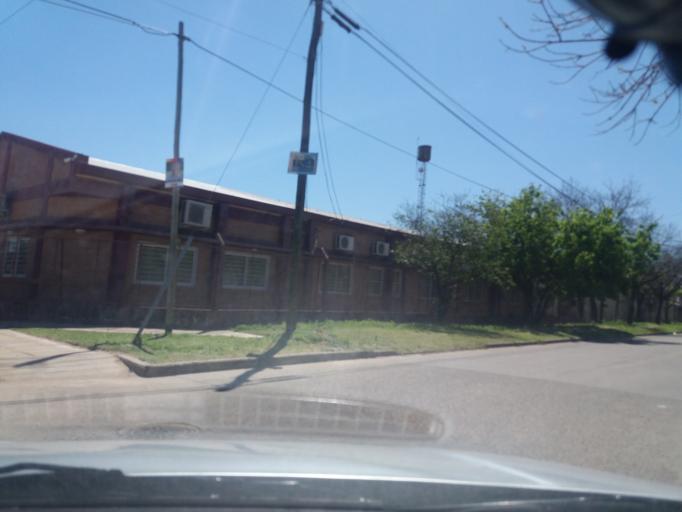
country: AR
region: Corrientes
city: Corrientes
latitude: -27.4882
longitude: -58.8448
